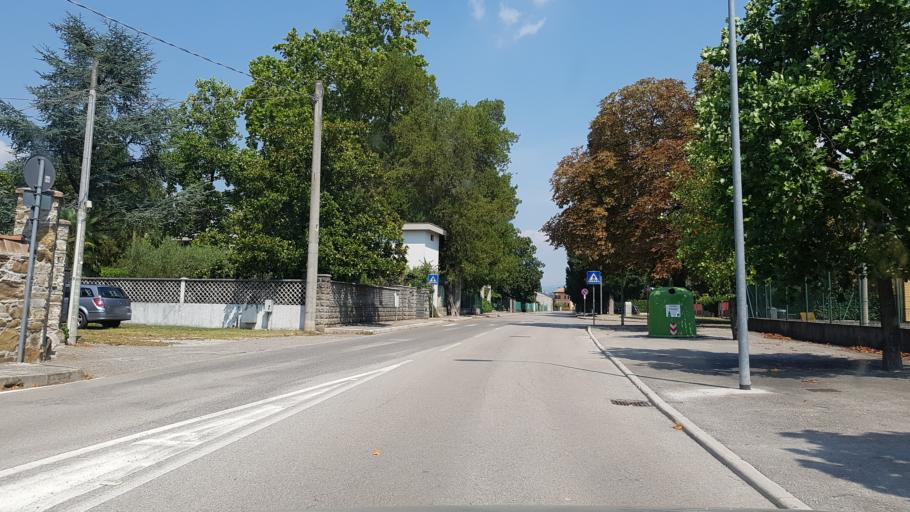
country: IT
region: Friuli Venezia Giulia
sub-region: Provincia di Gorizia
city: Farra d'Isonzo
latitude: 45.9107
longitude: 13.5155
